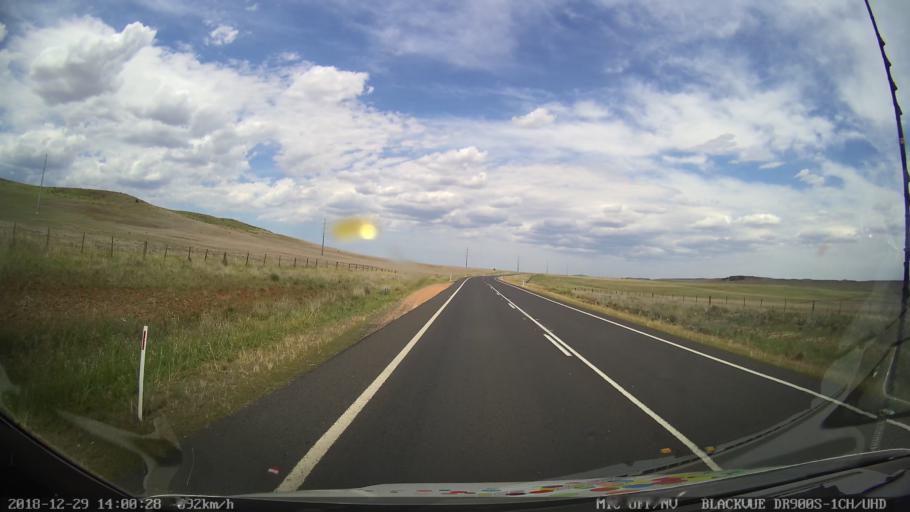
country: AU
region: New South Wales
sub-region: Cooma-Monaro
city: Cooma
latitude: -36.2641
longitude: 149.1590
